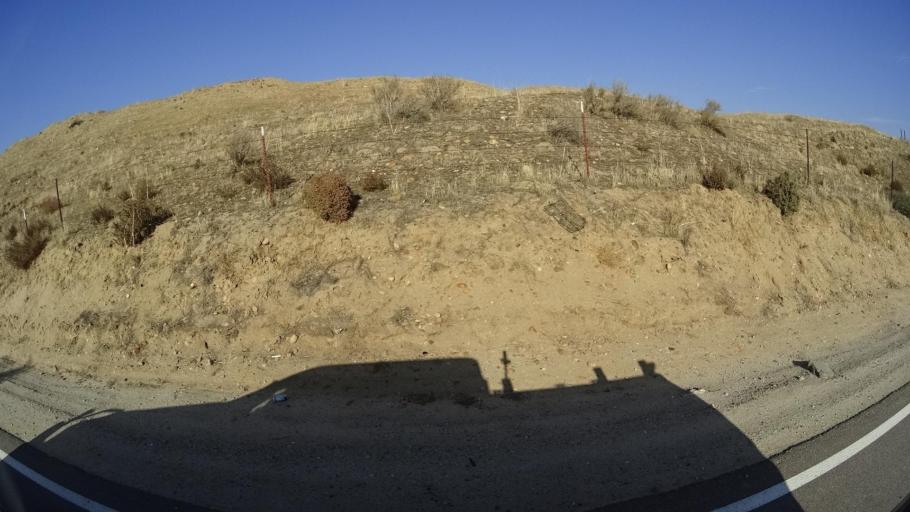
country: US
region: California
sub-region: Kern County
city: Oildale
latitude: 35.4497
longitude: -118.9230
